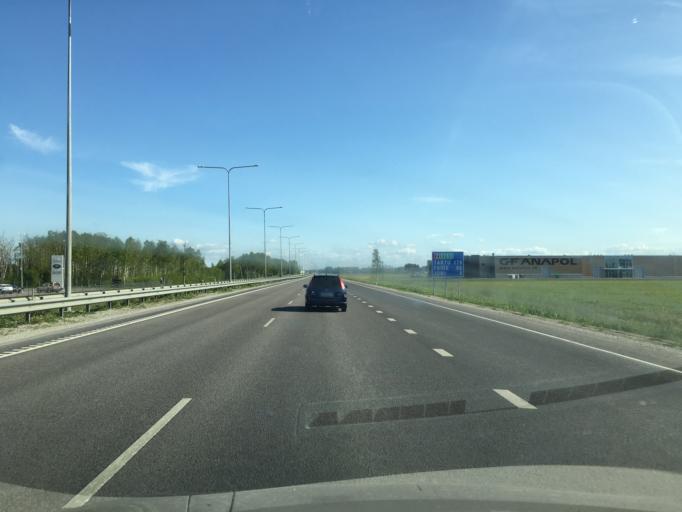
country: EE
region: Harju
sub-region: Rae vald
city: Jueri
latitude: 59.3941
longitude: 24.8231
